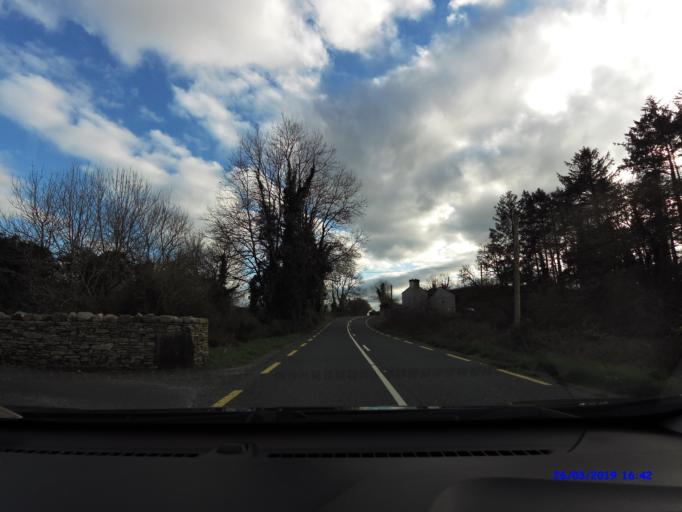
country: IE
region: Connaught
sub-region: Maigh Eo
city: Ballyhaunis
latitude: 53.8614
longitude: -8.7646
